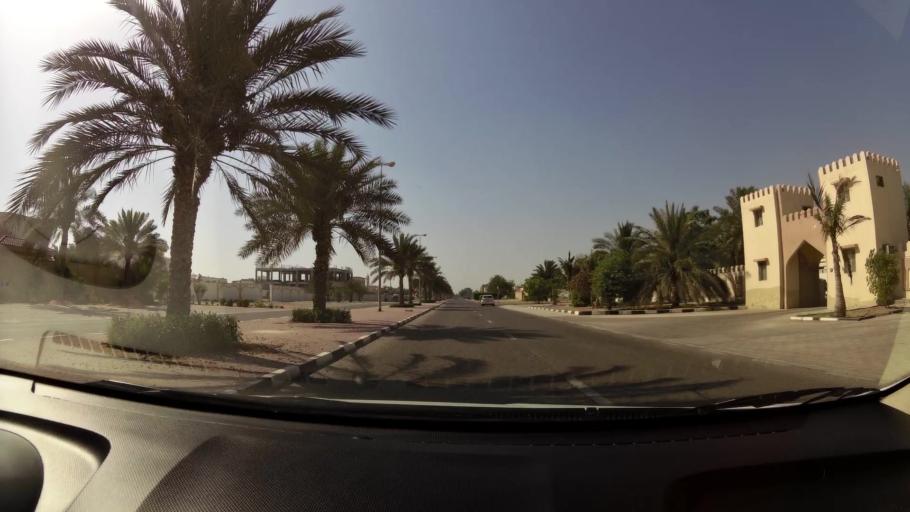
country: AE
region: Ajman
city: Ajman
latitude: 25.4145
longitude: 55.4666
